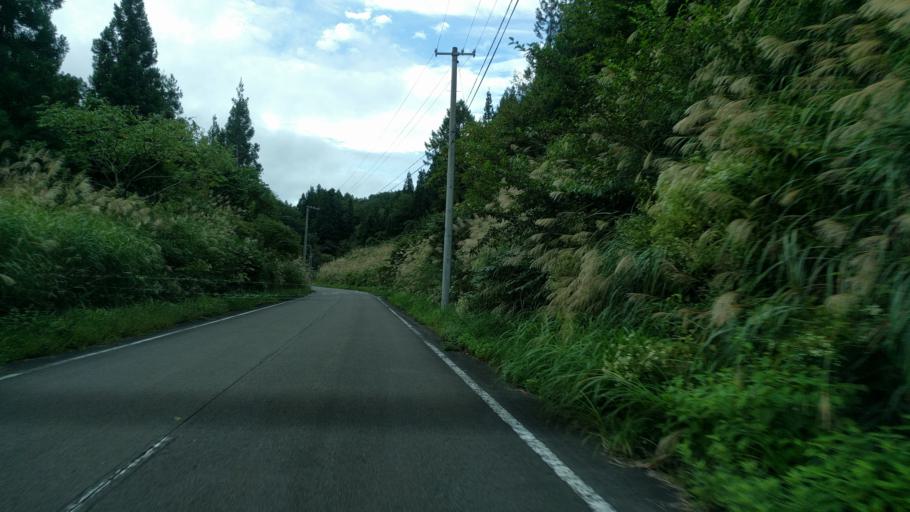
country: JP
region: Fukushima
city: Kitakata
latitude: 37.5081
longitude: 139.7628
